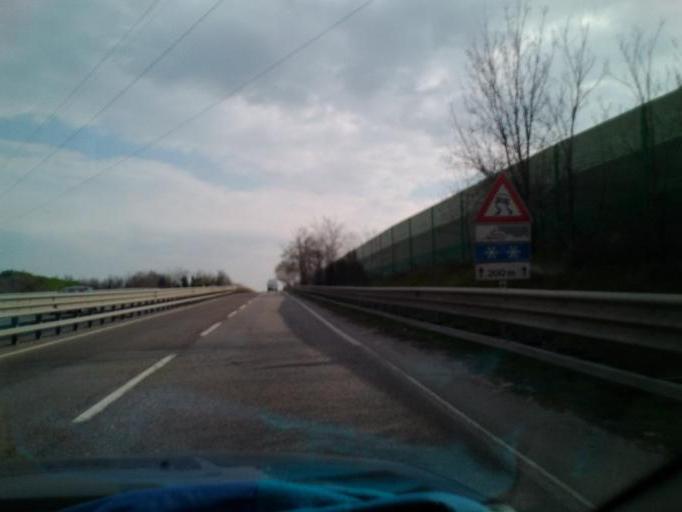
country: IT
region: Veneto
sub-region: Provincia di Verona
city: Bussolengo
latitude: 45.4767
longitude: 10.8606
